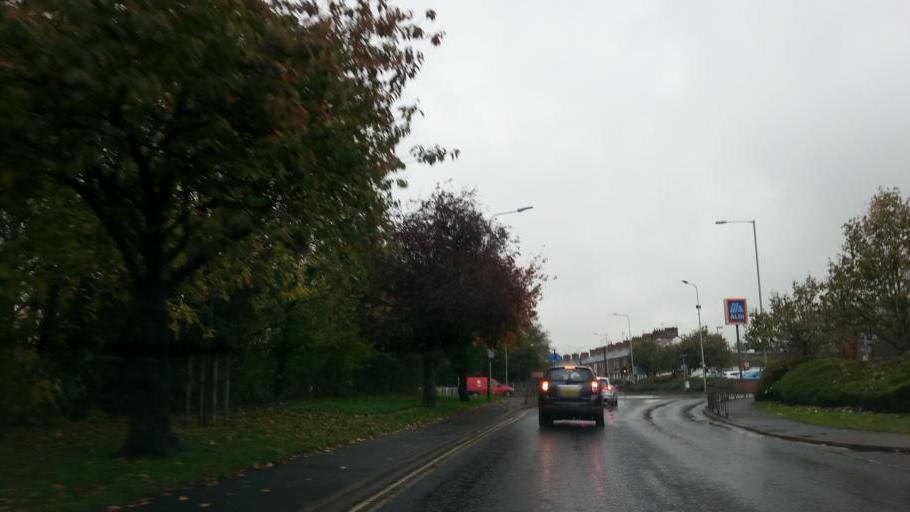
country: GB
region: England
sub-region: Suffolk
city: Haverhill
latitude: 52.0826
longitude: 0.4412
